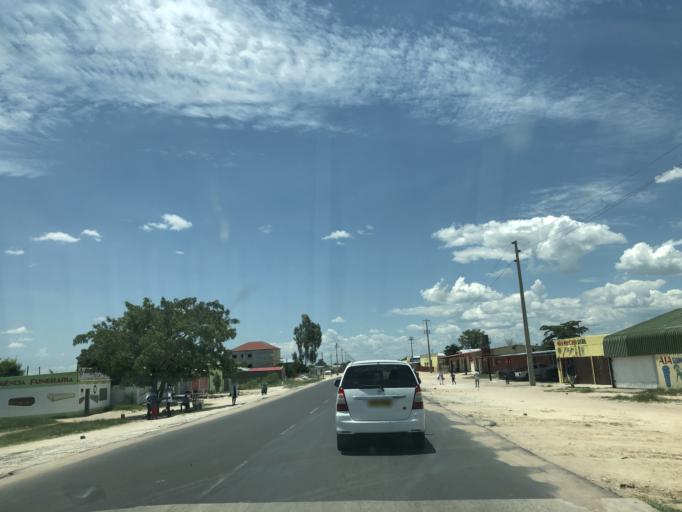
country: AO
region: Cunene
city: Ondjiva
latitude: -17.0544
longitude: 15.7419
